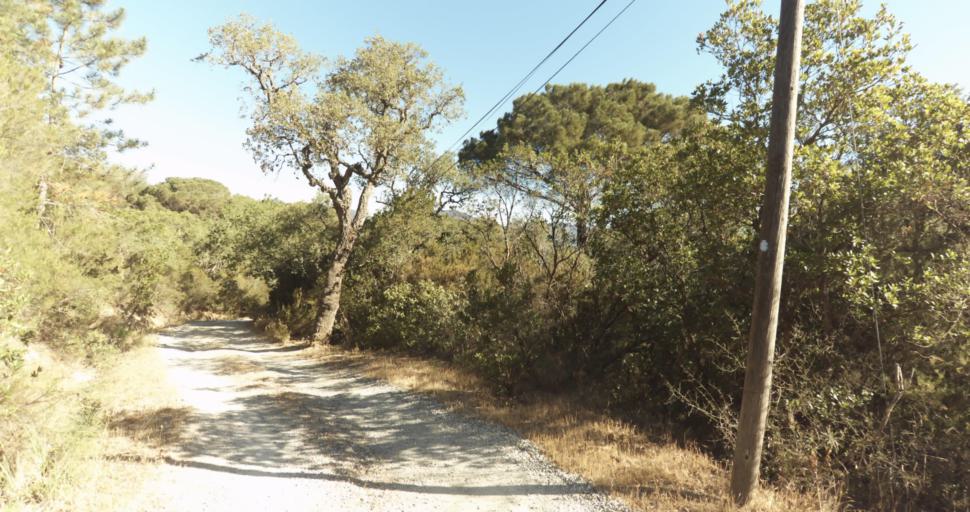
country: FR
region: Provence-Alpes-Cote d'Azur
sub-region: Departement du Var
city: Saint-Tropez
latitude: 43.2559
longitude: 6.6217
